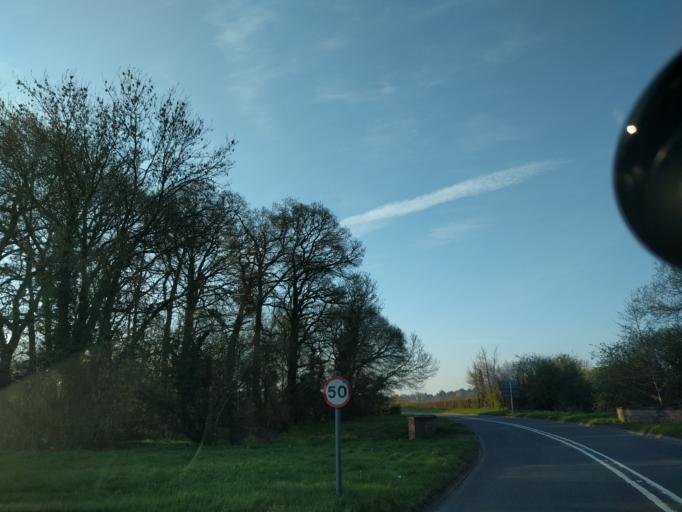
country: GB
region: England
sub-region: Wiltshire
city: Market Lavington
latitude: 51.3009
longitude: -2.0092
